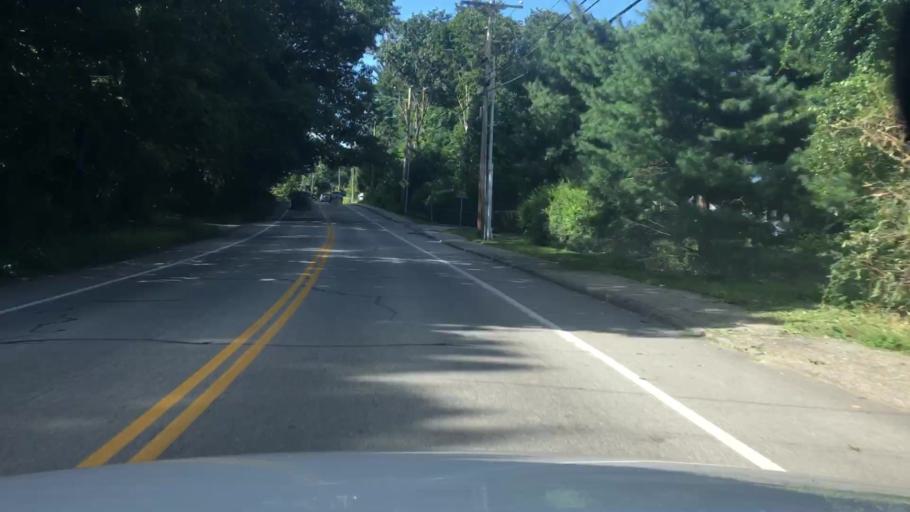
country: US
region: New Hampshire
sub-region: Strafford County
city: Dover
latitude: 43.1719
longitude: -70.8730
